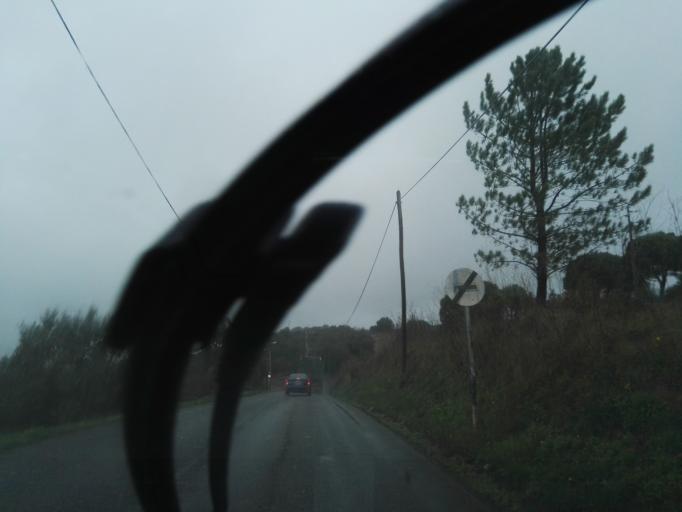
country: PT
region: Lisbon
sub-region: Loures
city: Bucelas
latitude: 38.9141
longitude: -9.0785
